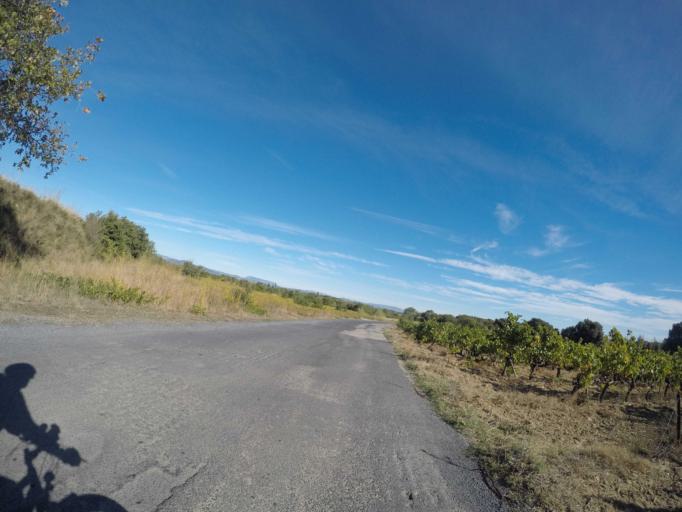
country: FR
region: Languedoc-Roussillon
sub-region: Departement des Pyrenees-Orientales
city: Trouillas
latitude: 42.6038
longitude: 2.8052
